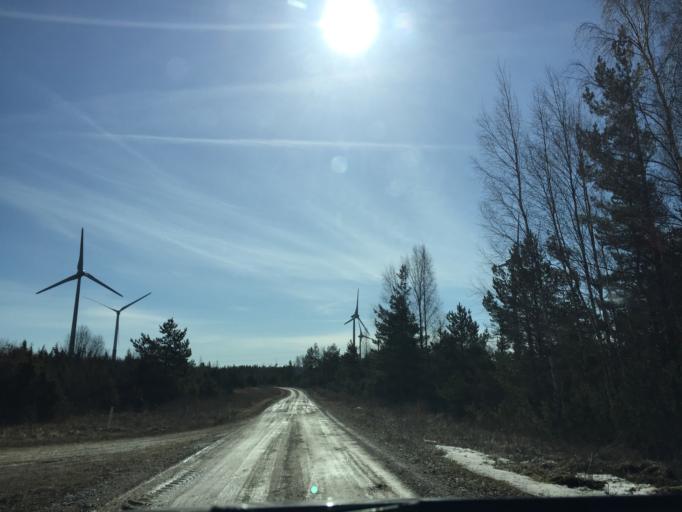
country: EE
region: Laeaene
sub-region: Haapsalu linn
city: Haapsalu
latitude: 58.6365
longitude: 23.5214
